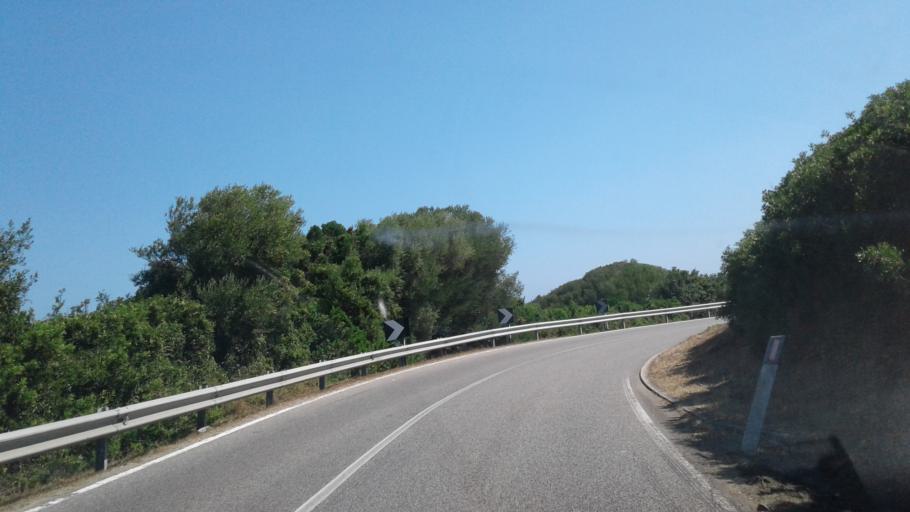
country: IT
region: Sardinia
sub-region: Provincia di Olbia-Tempio
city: Palau
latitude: 41.1708
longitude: 9.3242
